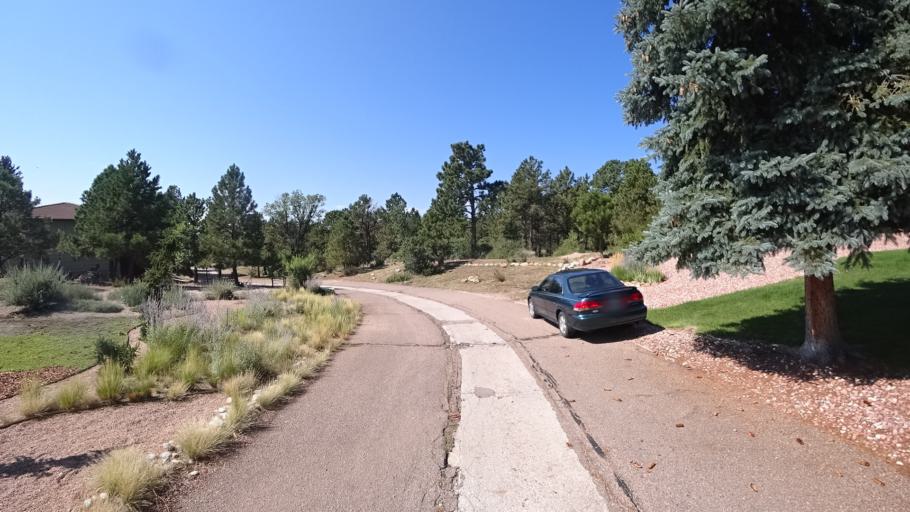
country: US
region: Colorado
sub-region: El Paso County
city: Air Force Academy
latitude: 38.9263
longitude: -104.8217
